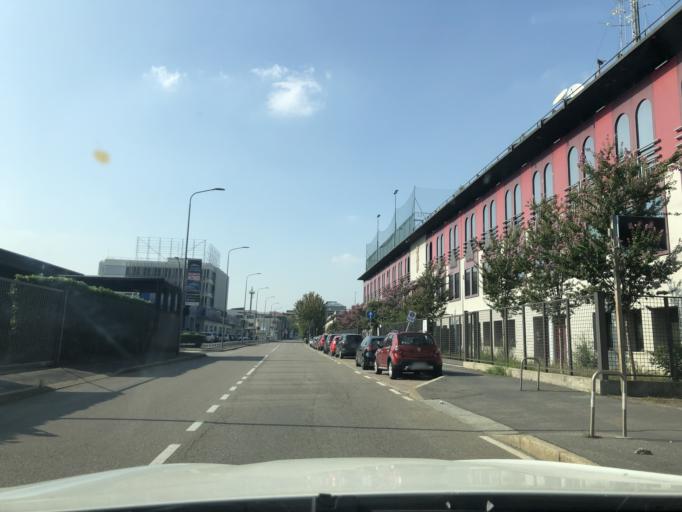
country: IT
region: Lombardy
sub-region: Citta metropolitana di Milano
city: Baranzate
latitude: 45.4983
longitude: 9.1287
